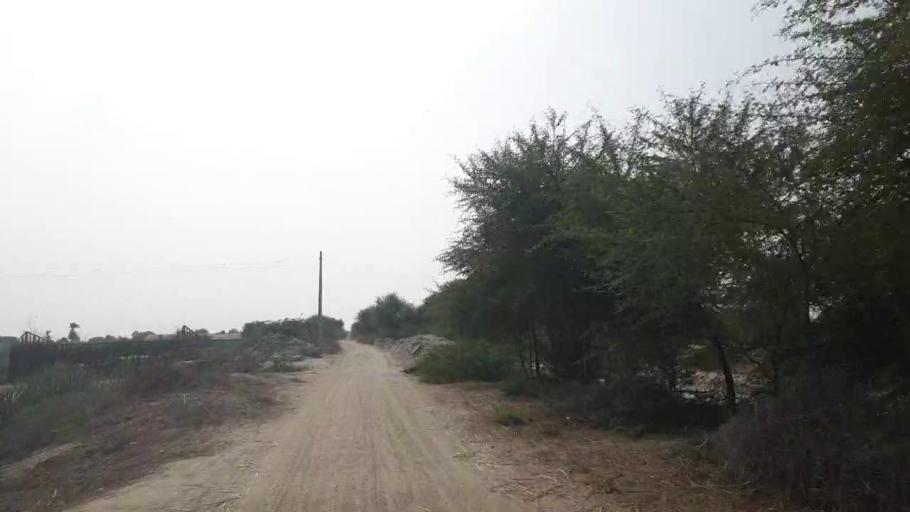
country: PK
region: Sindh
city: Badin
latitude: 24.6132
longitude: 68.7220
